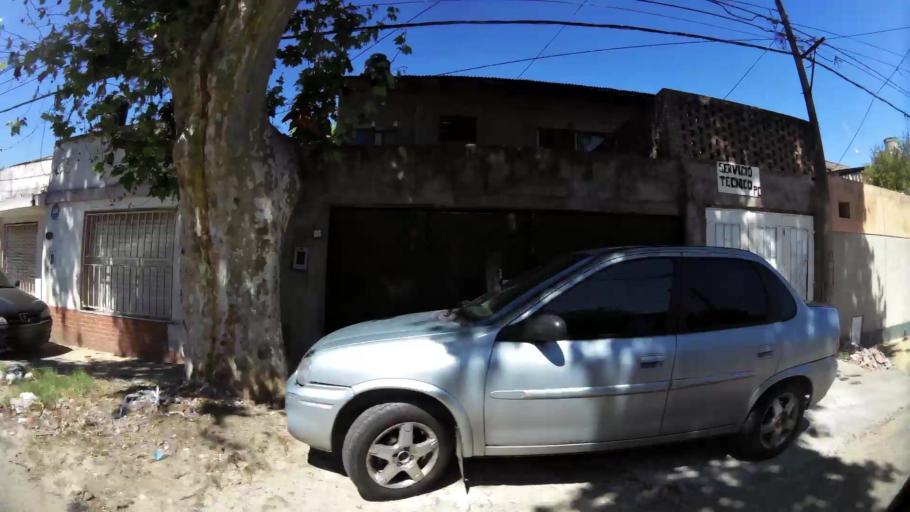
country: AR
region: Santa Fe
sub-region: Departamento de Rosario
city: Rosario
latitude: -32.9338
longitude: -60.6920
